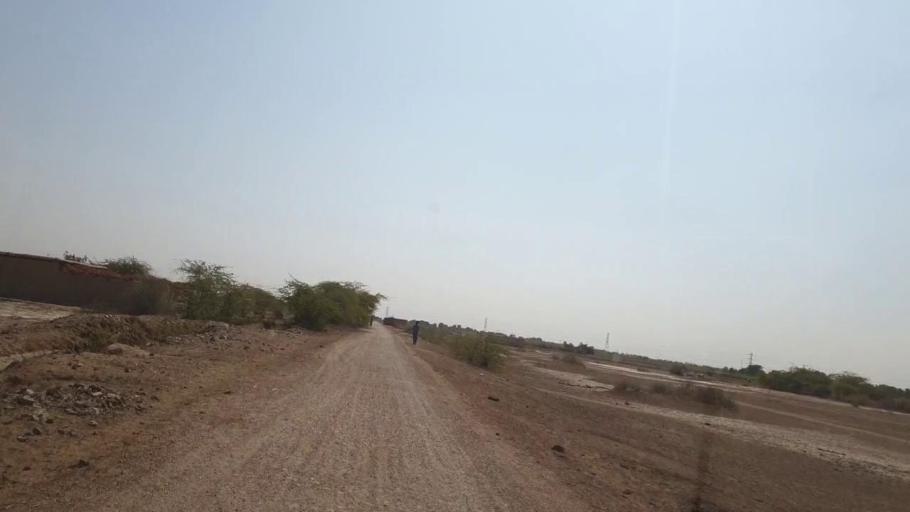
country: PK
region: Sindh
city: Nabisar
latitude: 25.0741
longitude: 69.5487
